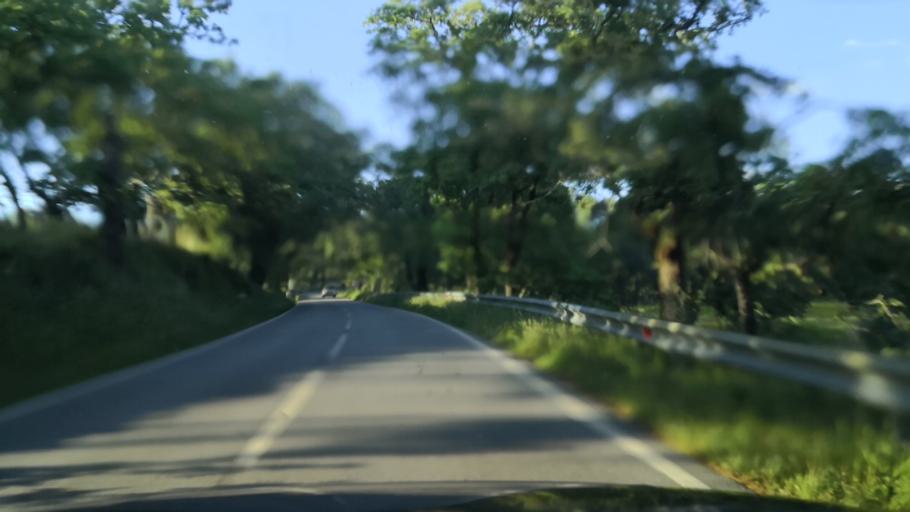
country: PT
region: Portalegre
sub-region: Portalegre
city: Portalegre
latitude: 39.3344
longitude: -7.4218
